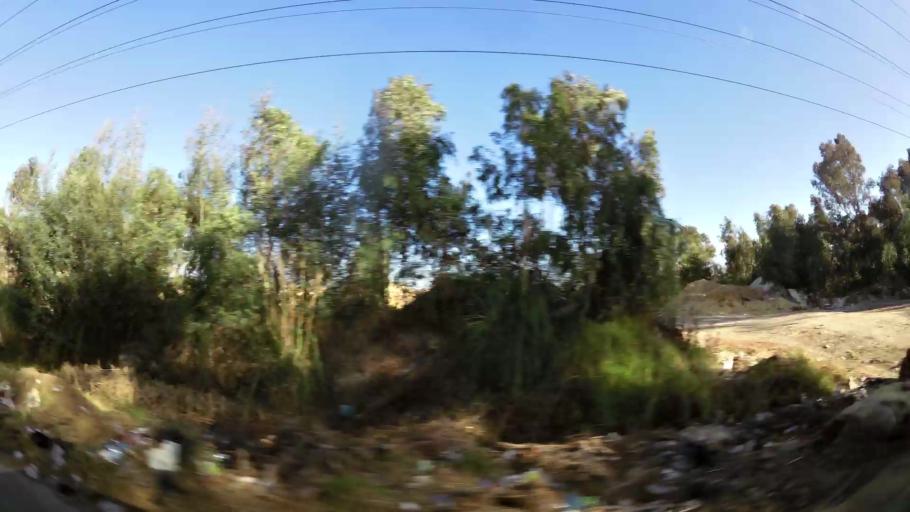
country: ZA
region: Gauteng
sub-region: City of Johannesburg Metropolitan Municipality
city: Roodepoort
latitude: -26.1581
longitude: 27.8578
